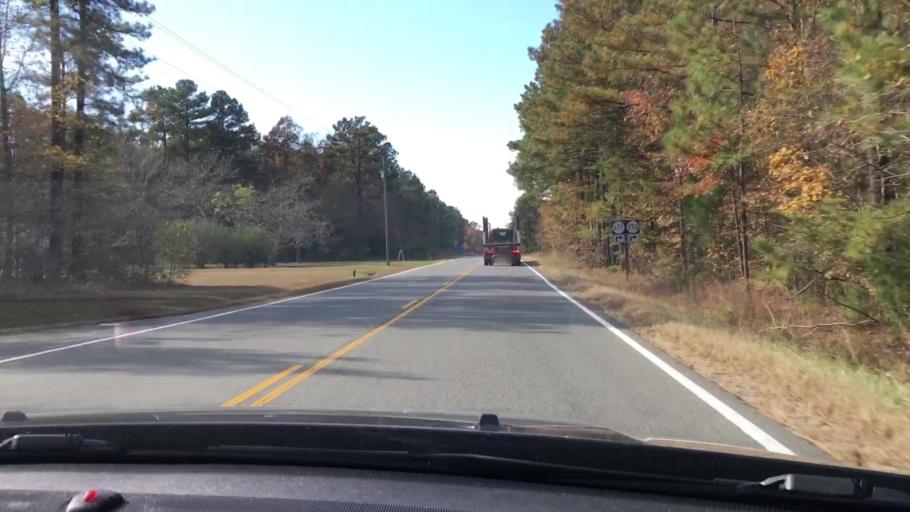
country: US
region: Virginia
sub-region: Hanover County
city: Hanover
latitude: 37.8259
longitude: -77.3362
